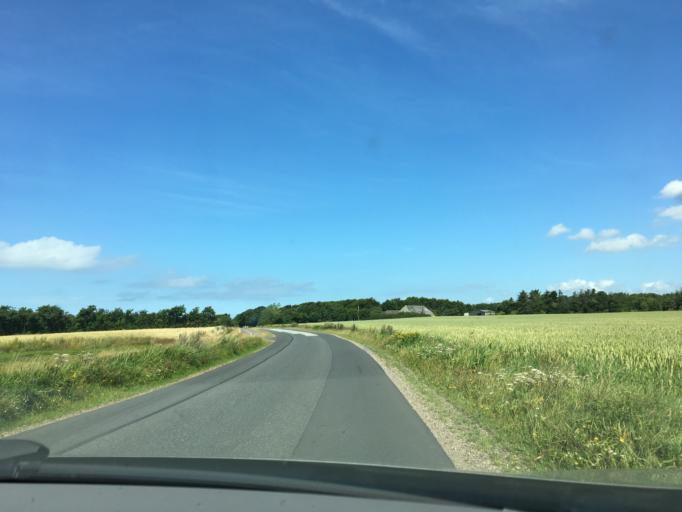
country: DK
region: Central Jutland
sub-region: Ringkobing-Skjern Kommune
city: Ringkobing
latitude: 55.9815
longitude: 8.3481
